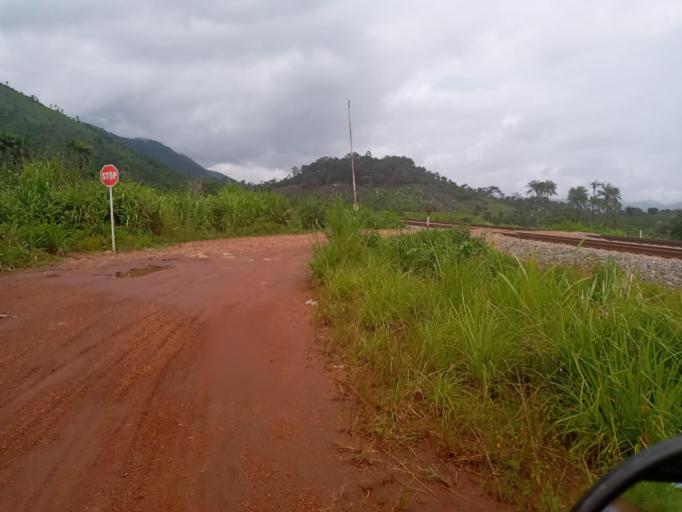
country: SL
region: Northern Province
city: Bumbuna
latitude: 8.9696
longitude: -11.7540
